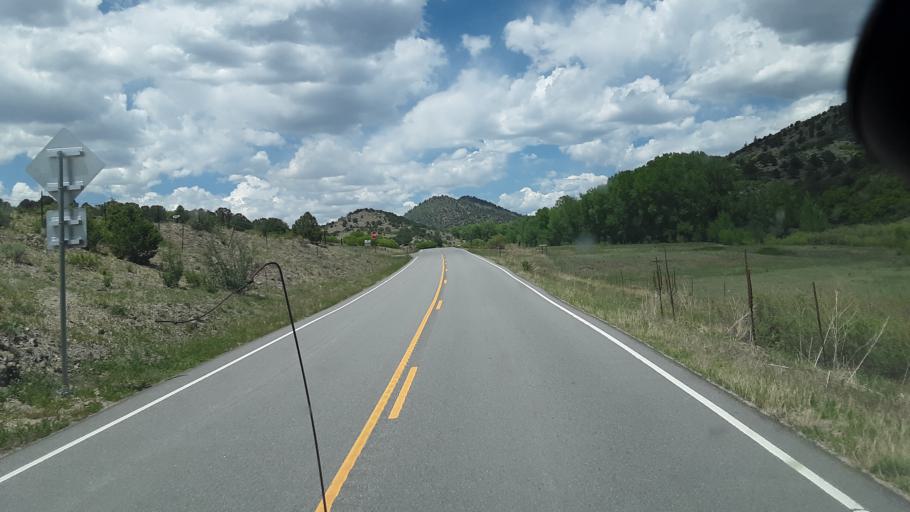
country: US
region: Colorado
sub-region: Teller County
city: Cripple Creek
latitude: 38.6721
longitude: -105.4878
